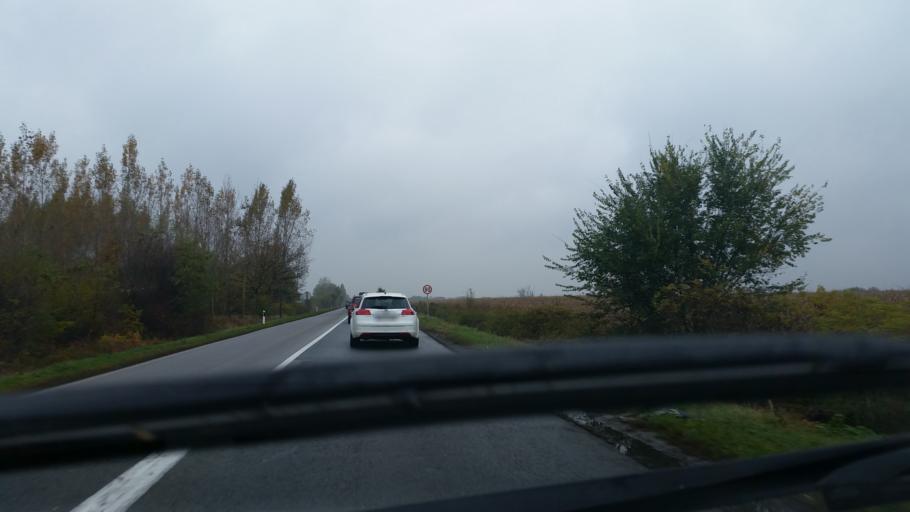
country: RS
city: Sefkerin
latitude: 44.9358
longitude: 20.4367
